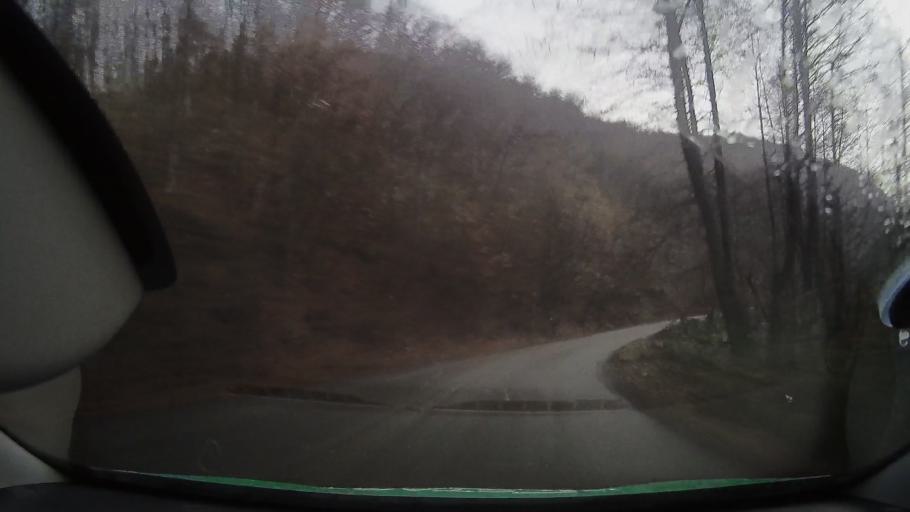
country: RO
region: Hunedoara
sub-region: Comuna Ribita
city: Ribita
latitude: 46.2835
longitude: 22.7361
